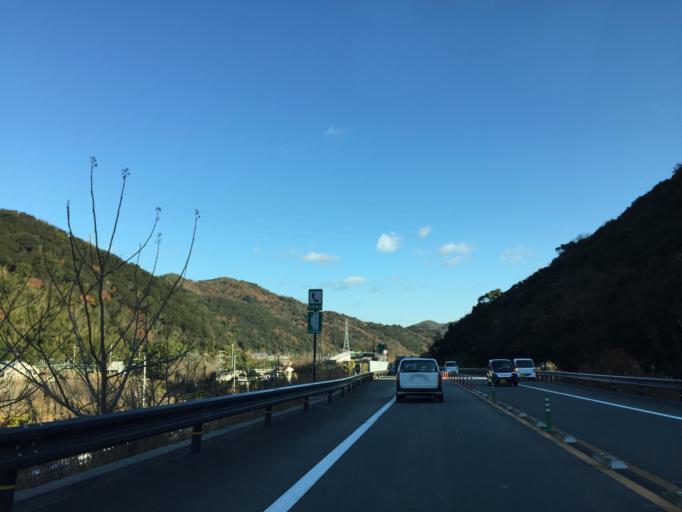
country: JP
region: Wakayama
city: Wakayama-shi
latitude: 34.2938
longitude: 135.1520
